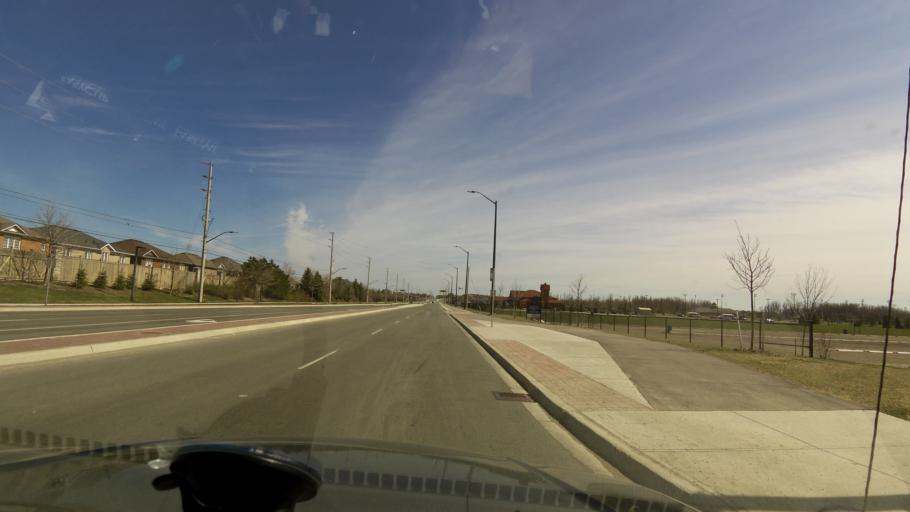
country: CA
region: Ontario
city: Brampton
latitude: 43.6886
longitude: -79.8355
